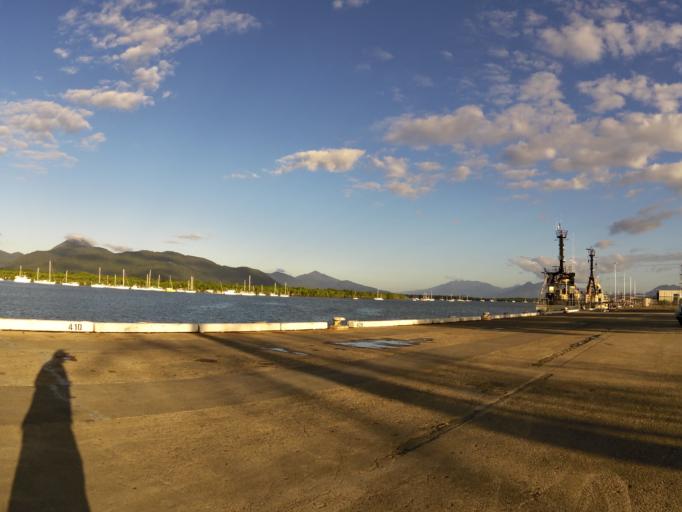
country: AU
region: Queensland
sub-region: Cairns
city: Cairns
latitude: -16.9280
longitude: 145.7799
